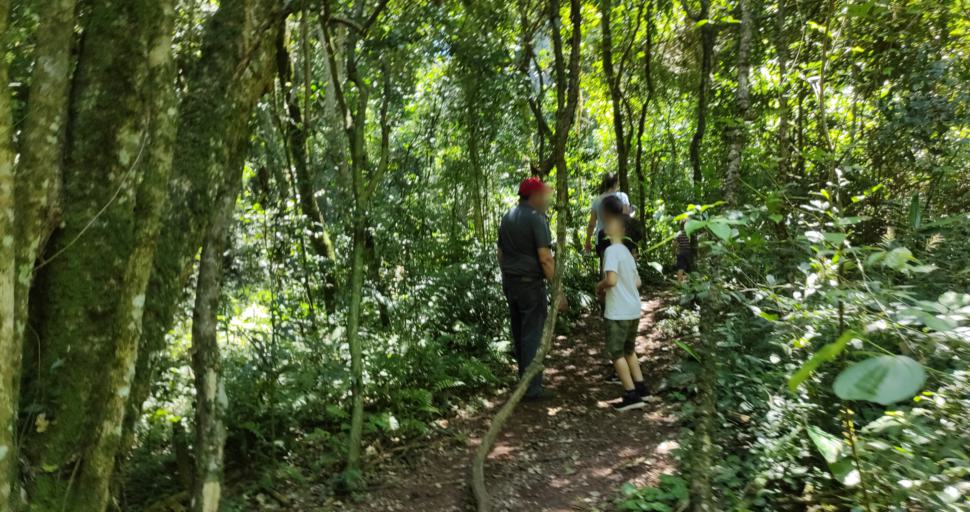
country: BR
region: Rio Grande do Sul
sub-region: Tres Passos
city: Tres Passos
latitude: -27.1503
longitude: -53.9002
